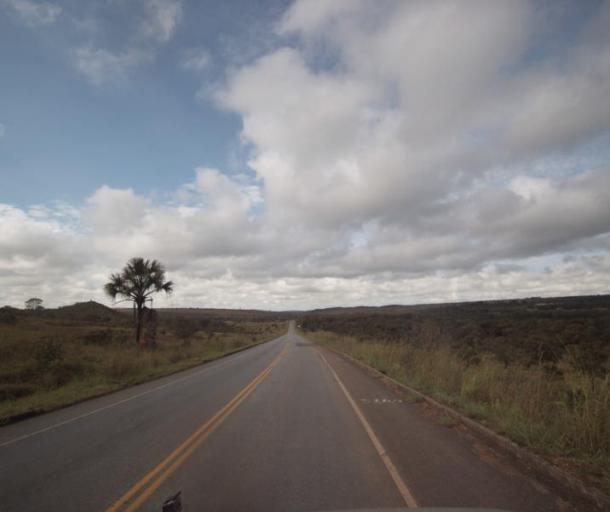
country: BR
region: Goias
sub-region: Pirenopolis
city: Pirenopolis
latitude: -15.8120
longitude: -48.7822
